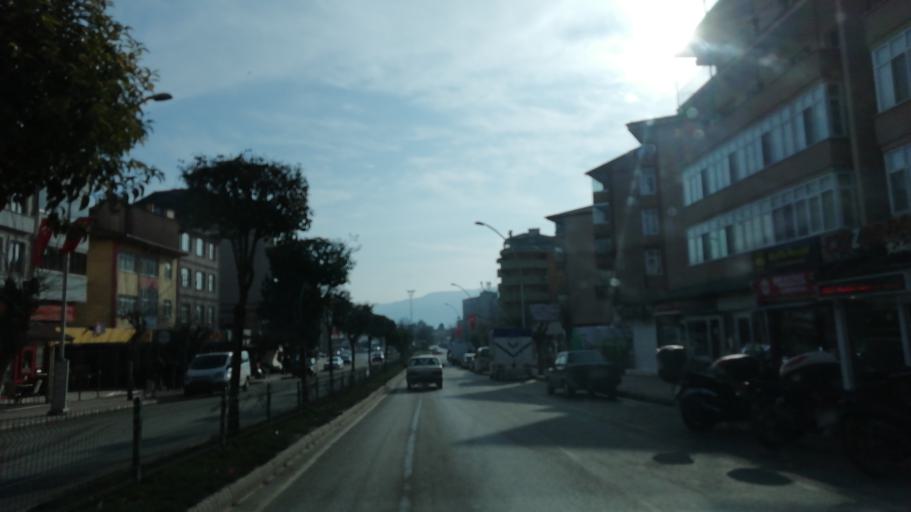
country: TR
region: Karabuk
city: Safranbolu
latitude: 41.2521
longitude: 32.6801
